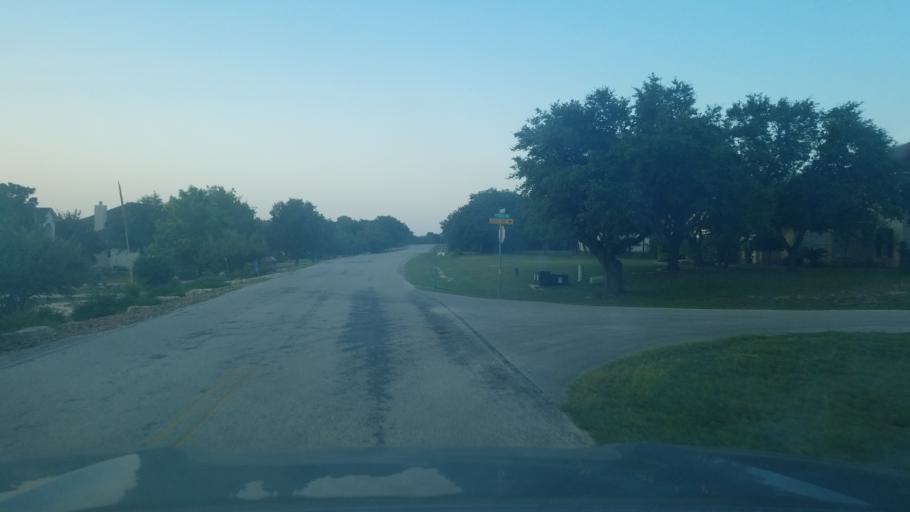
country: US
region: Texas
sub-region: Comal County
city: Bulverde
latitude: 29.8309
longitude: -98.4037
